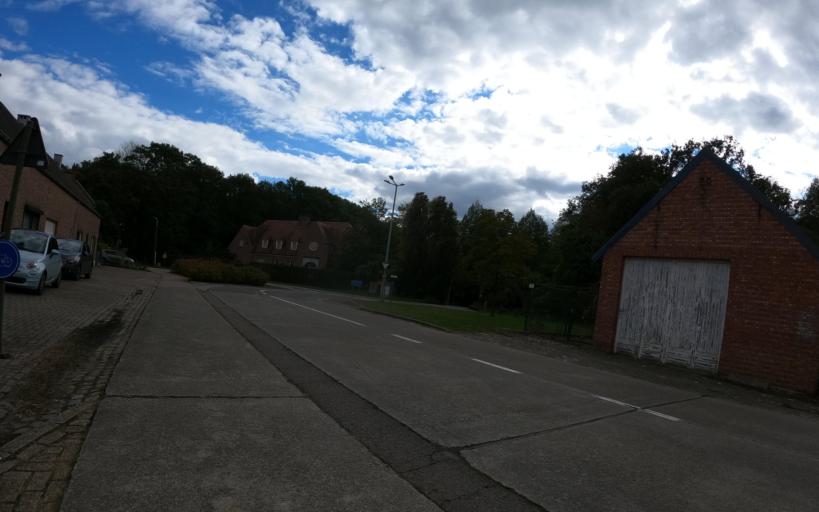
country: BE
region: Flanders
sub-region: Provincie Antwerpen
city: Heist-op-den-Berg
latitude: 51.1048
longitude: 4.7122
